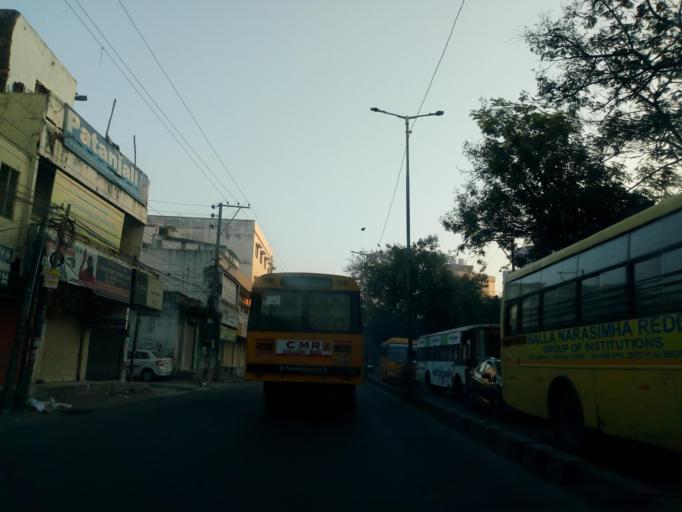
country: IN
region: Telangana
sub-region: Rangareddi
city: Gaddi Annaram
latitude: 17.3964
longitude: 78.5035
